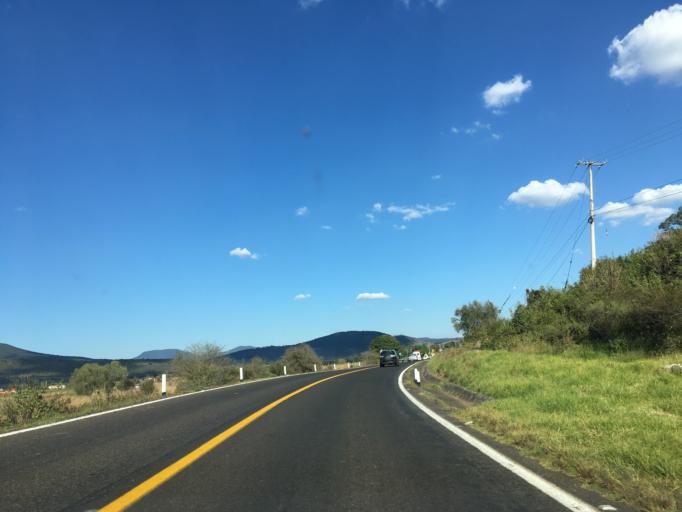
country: MX
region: Michoacan
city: Patzcuaro
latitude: 19.5653
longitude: -101.5758
